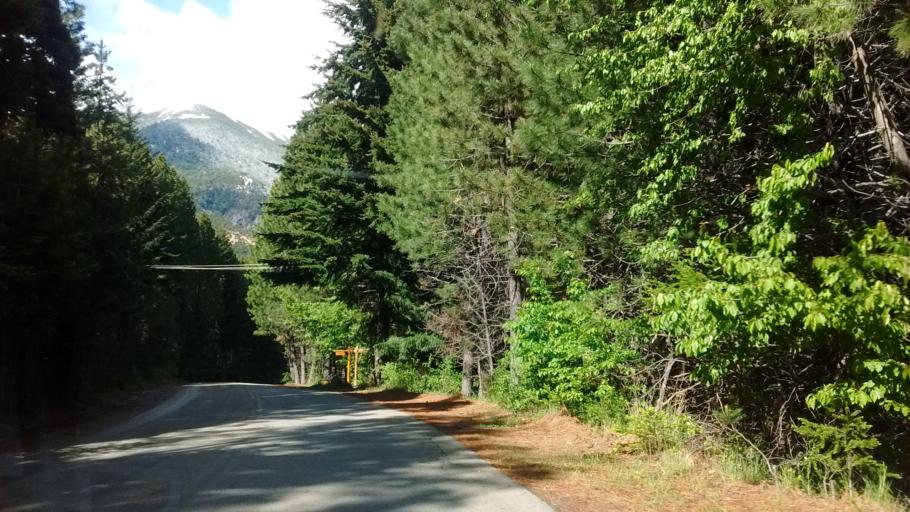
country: AR
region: Rio Negro
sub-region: Departamento de Bariloche
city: San Carlos de Bariloche
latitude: -41.0741
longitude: -71.5449
